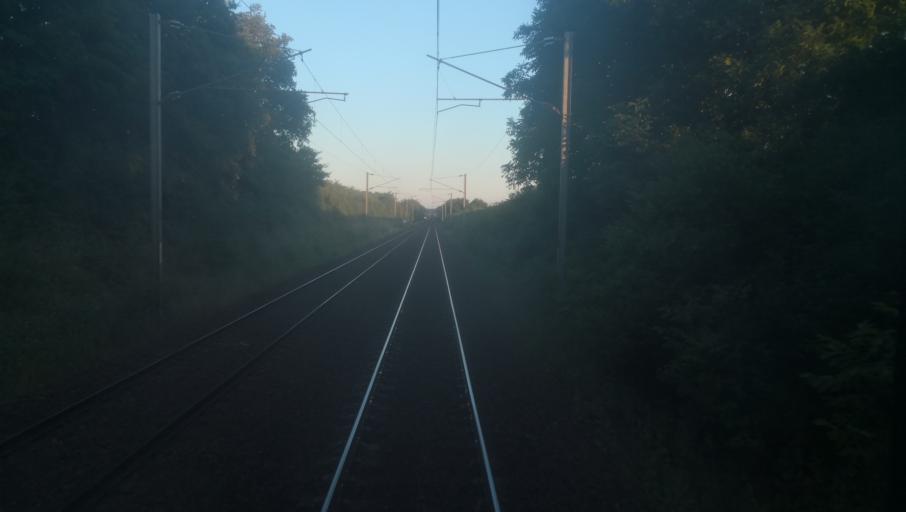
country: FR
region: Centre
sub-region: Departement du Cher
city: Herry
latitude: 47.2482
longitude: 3.0031
